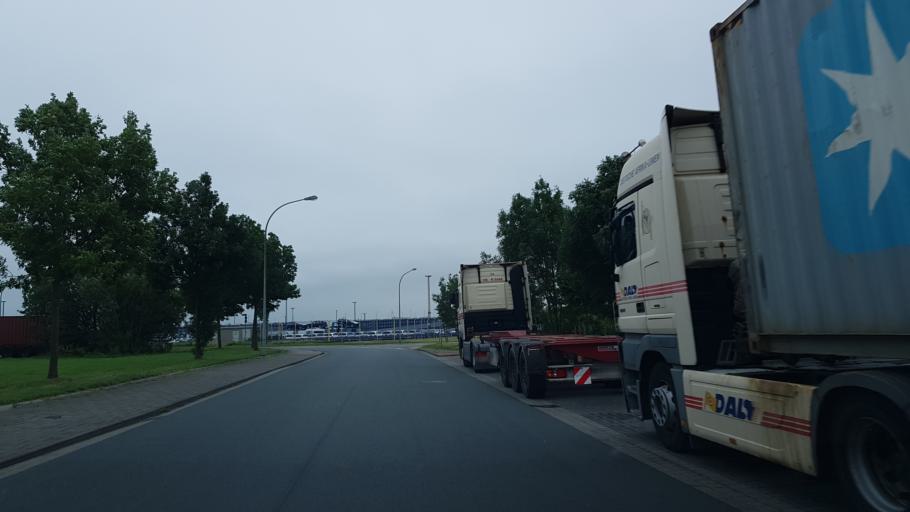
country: DE
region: Bremen
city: Bremerhaven
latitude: 53.5868
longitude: 8.5522
